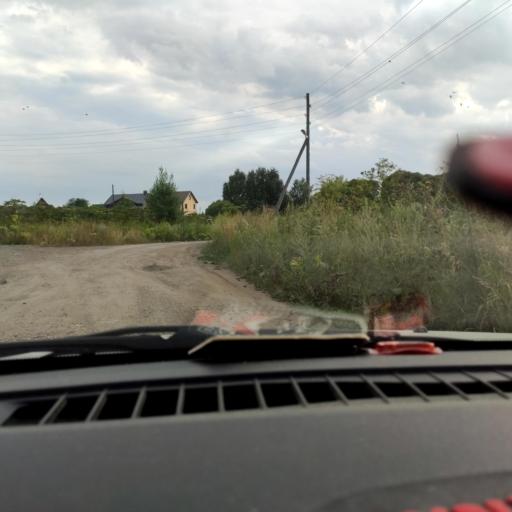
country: RU
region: Perm
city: Kultayevo
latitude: 57.8577
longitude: 55.9697
